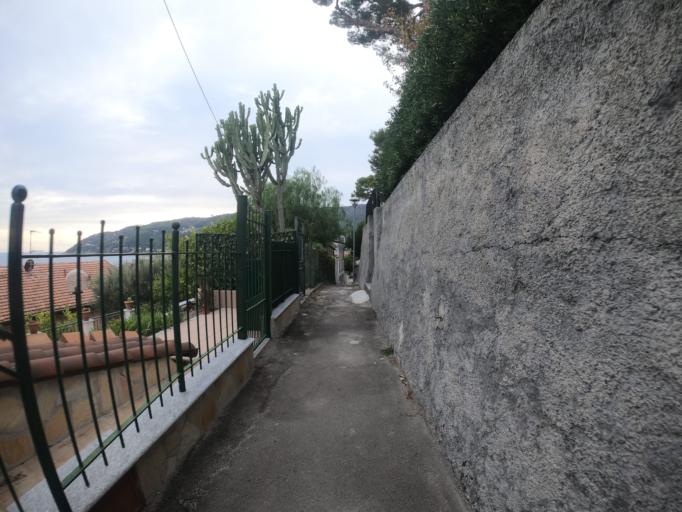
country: IT
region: Liguria
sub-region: Provincia di Savona
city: Marina di Andora
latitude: 43.9531
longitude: 8.1536
